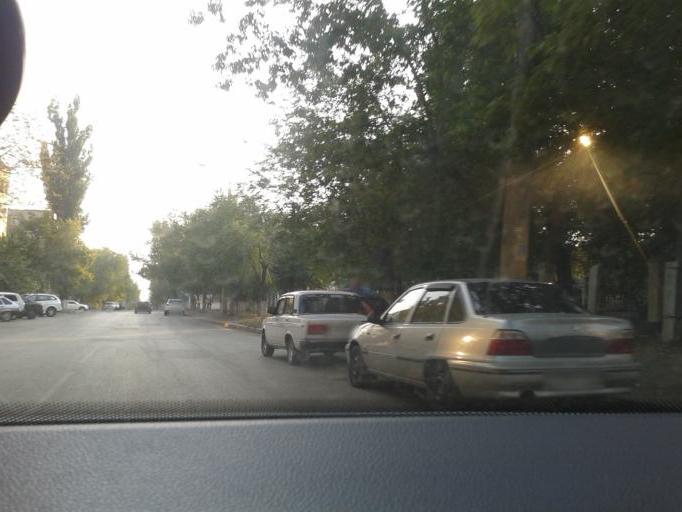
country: RU
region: Volgograd
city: Volgograd
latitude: 48.7009
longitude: 44.5001
